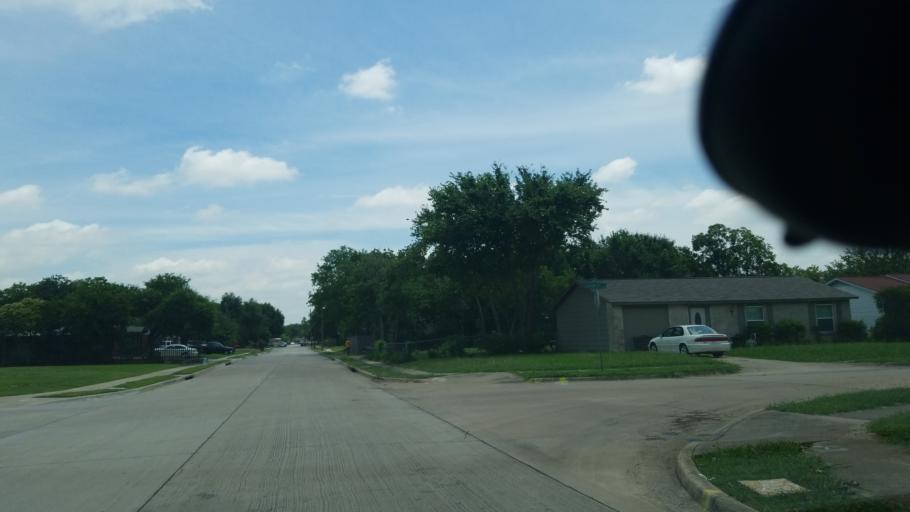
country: US
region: Texas
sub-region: Dallas County
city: Irving
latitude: 32.8465
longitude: -96.9642
